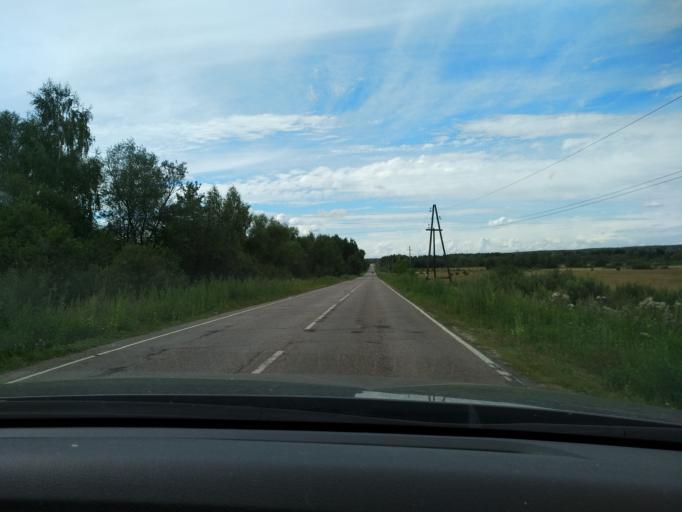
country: RU
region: Moskovskaya
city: Krasnyy Tkach
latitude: 55.3844
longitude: 39.1829
